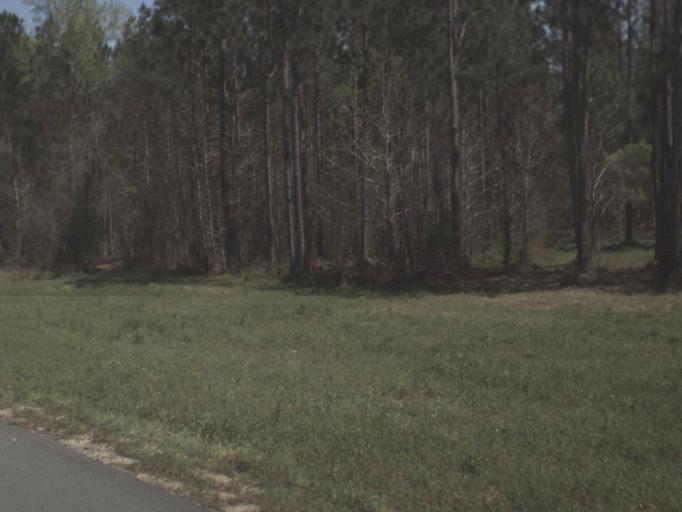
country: US
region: Florida
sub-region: Calhoun County
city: Blountstown
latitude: 30.4357
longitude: -85.2249
